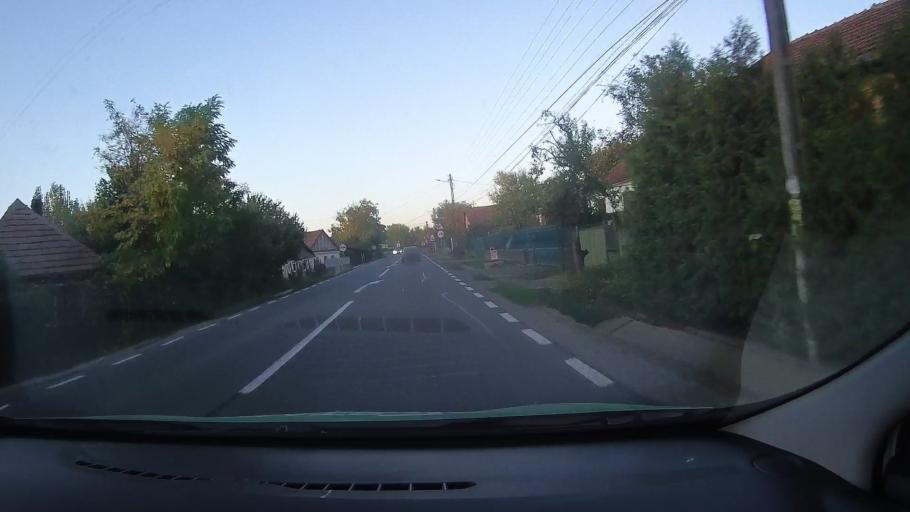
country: RO
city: Szekelyhid
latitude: 47.3348
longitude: 22.0873
